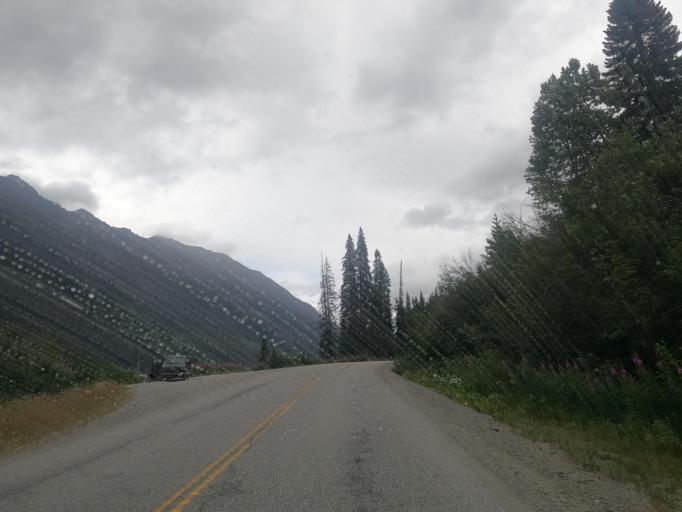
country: CA
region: British Columbia
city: Lillooet
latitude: 50.3998
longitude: -122.3135
